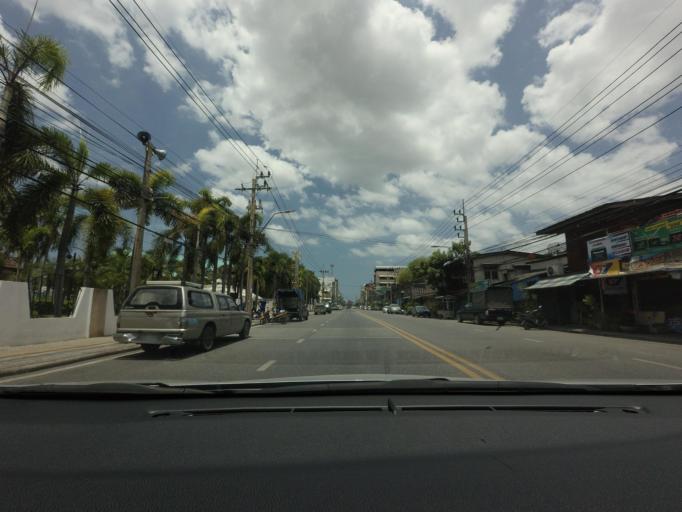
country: TH
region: Samut Prakan
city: Samut Prakan
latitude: 13.5882
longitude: 100.5960
